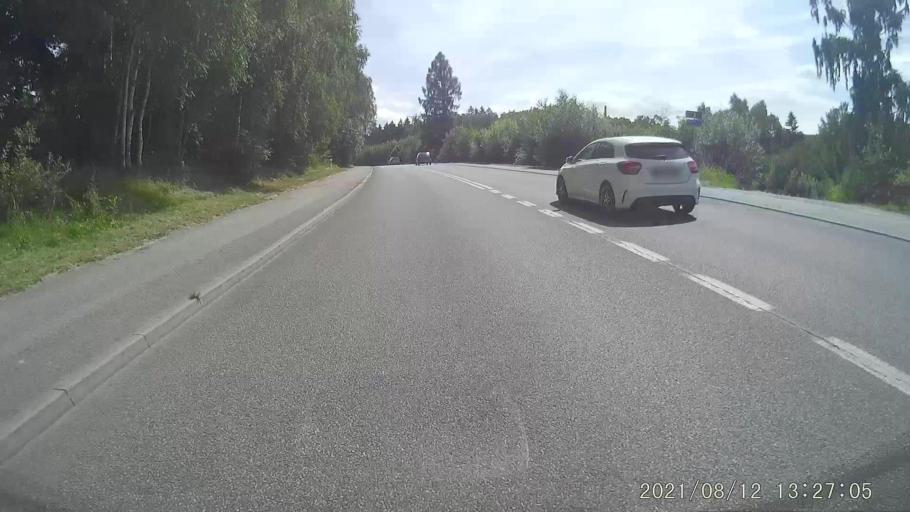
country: PL
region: Lower Silesian Voivodeship
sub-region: Powiat klodzki
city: Ladek-Zdroj
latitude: 50.3303
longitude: 16.8699
